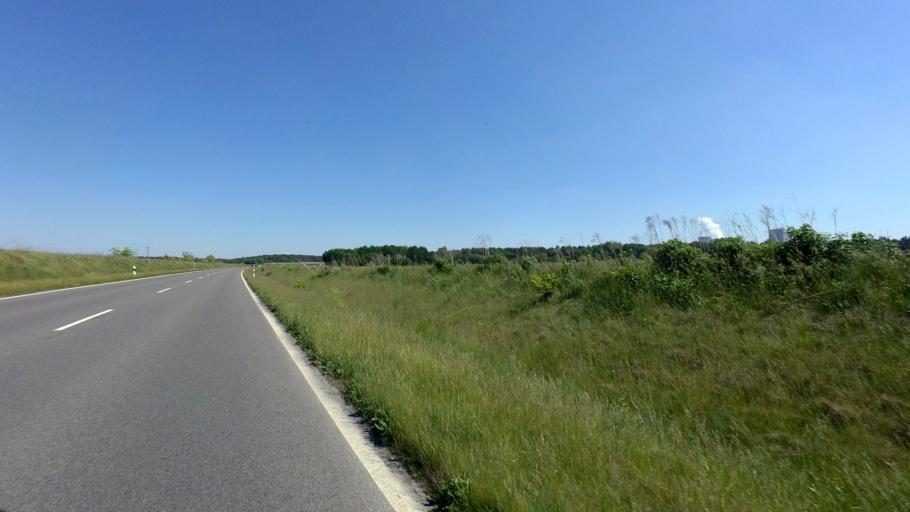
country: DE
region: Brandenburg
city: Spremberg
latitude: 51.5313
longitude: 14.3198
